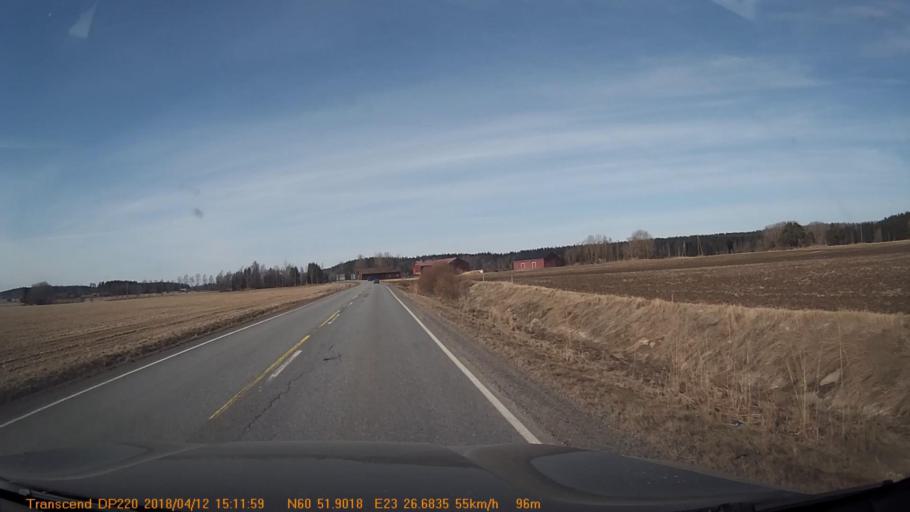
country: FI
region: Haeme
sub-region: Forssa
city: Jokioinen
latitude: 60.8652
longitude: 23.4446
